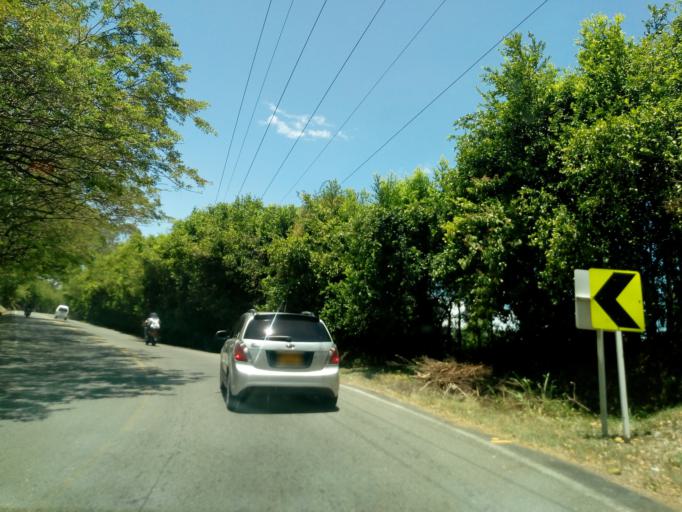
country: CO
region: Valle del Cauca
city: Cartago
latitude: 4.7277
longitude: -75.8924
